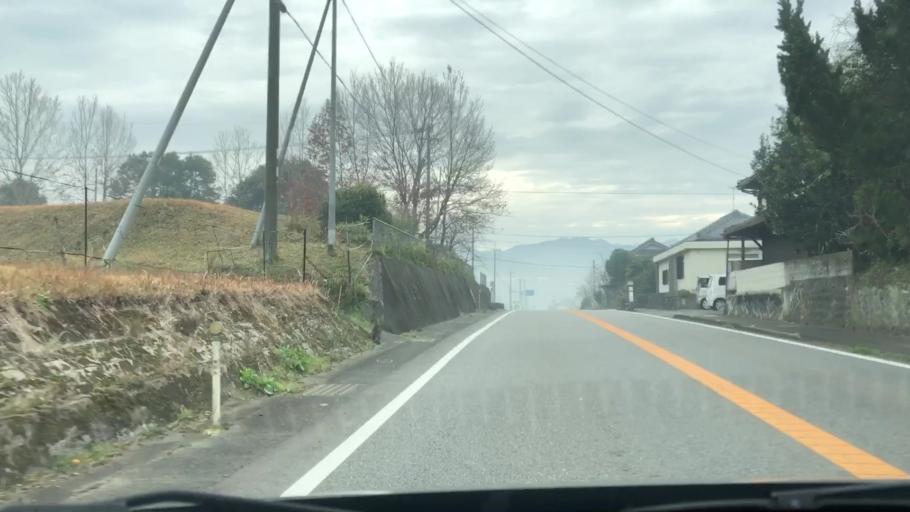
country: JP
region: Oita
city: Usuki
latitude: 33.0210
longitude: 131.6971
